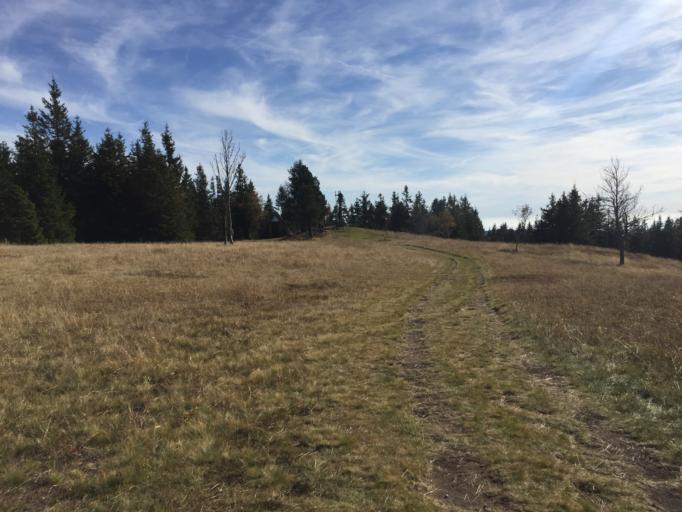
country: SI
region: Mislinja
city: Mislinja
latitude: 46.4863
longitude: 15.2329
